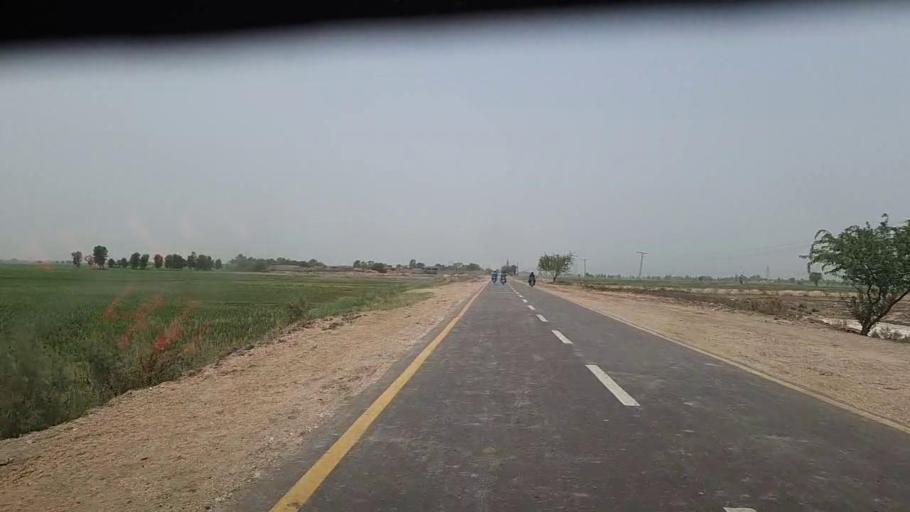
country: PK
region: Sindh
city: Sita Road
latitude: 27.0403
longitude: 67.8876
